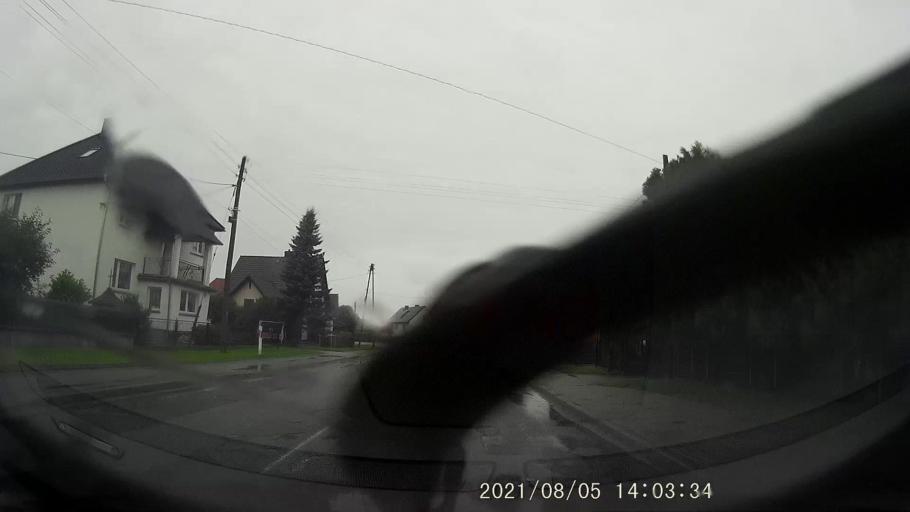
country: PL
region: Opole Voivodeship
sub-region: Powiat krapkowicki
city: Strzeleczki
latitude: 50.4581
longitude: 17.8564
